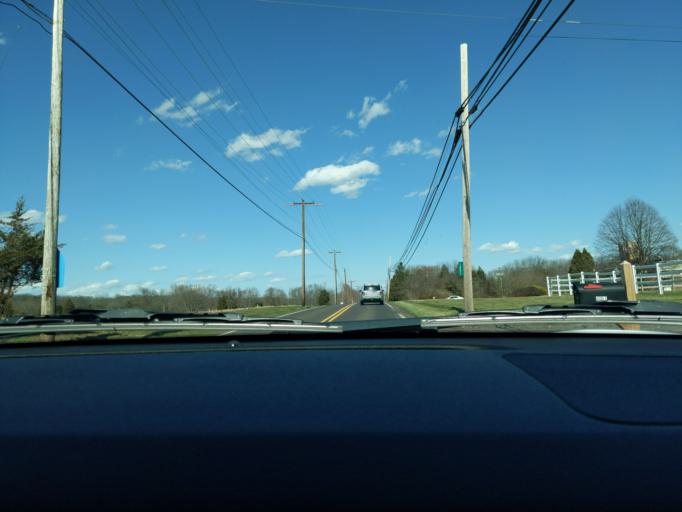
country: US
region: Pennsylvania
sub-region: Bucks County
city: Perkasie
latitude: 40.3971
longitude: -75.2610
